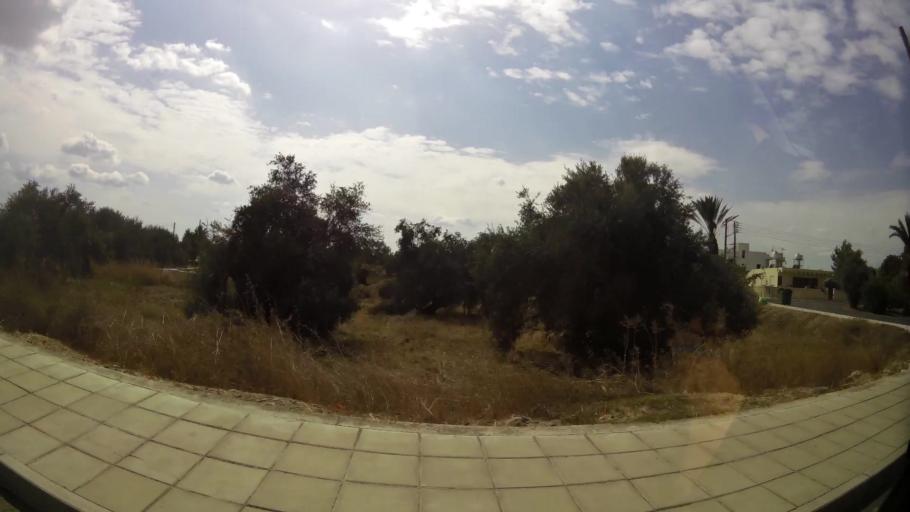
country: CY
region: Lefkosia
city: Tseri
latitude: 35.0721
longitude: 33.3274
